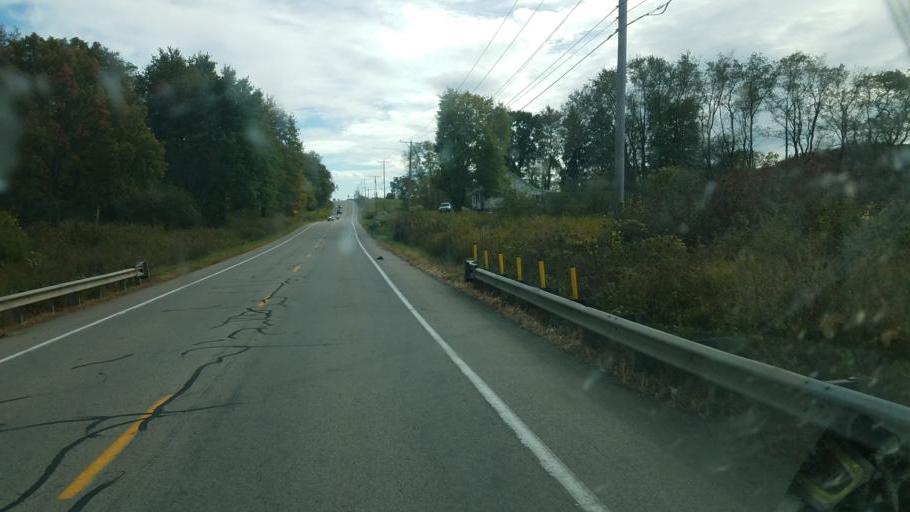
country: US
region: Pennsylvania
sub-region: Mercer County
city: Mercer
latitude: 41.2025
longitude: -80.2405
